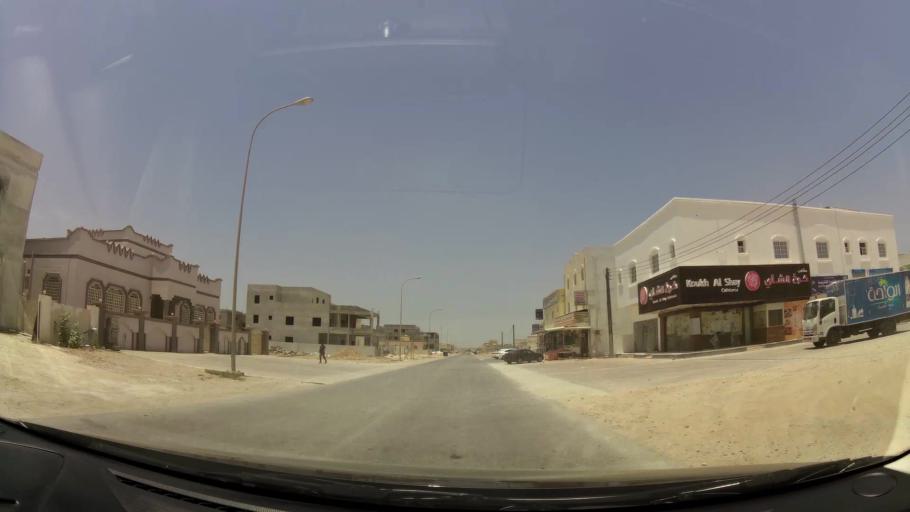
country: OM
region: Zufar
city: Salalah
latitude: 17.0926
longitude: 54.1560
